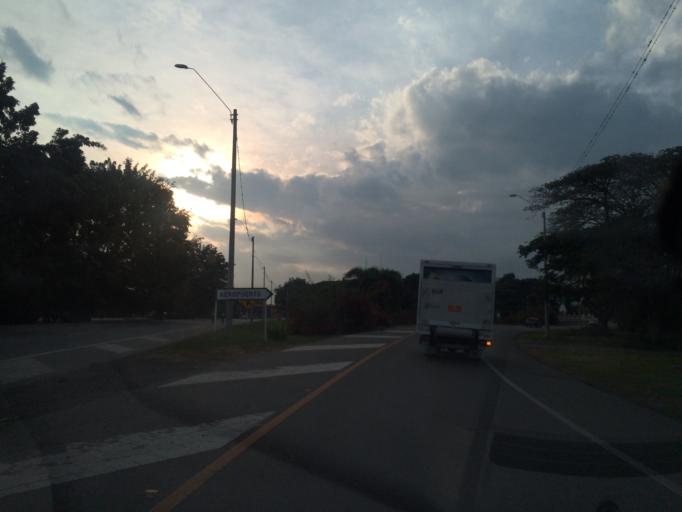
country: CO
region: Valle del Cauca
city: Palmira
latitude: 3.5112
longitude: -76.3977
